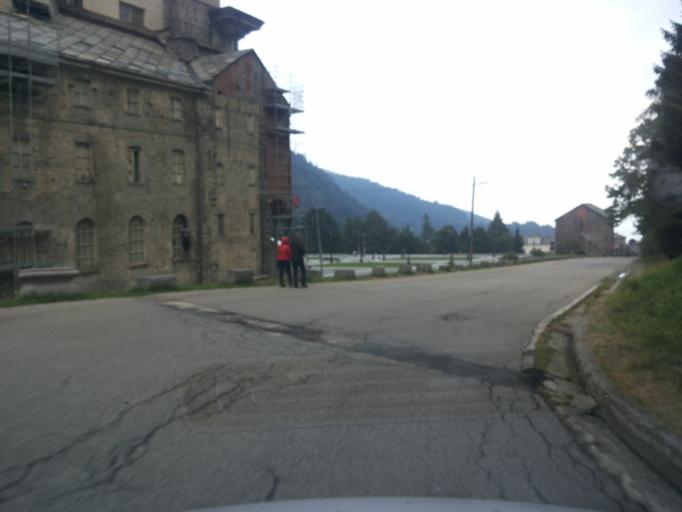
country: IT
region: Piedmont
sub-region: Provincia di Biella
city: Campiglia Cervo
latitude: 45.6287
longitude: 7.9771
